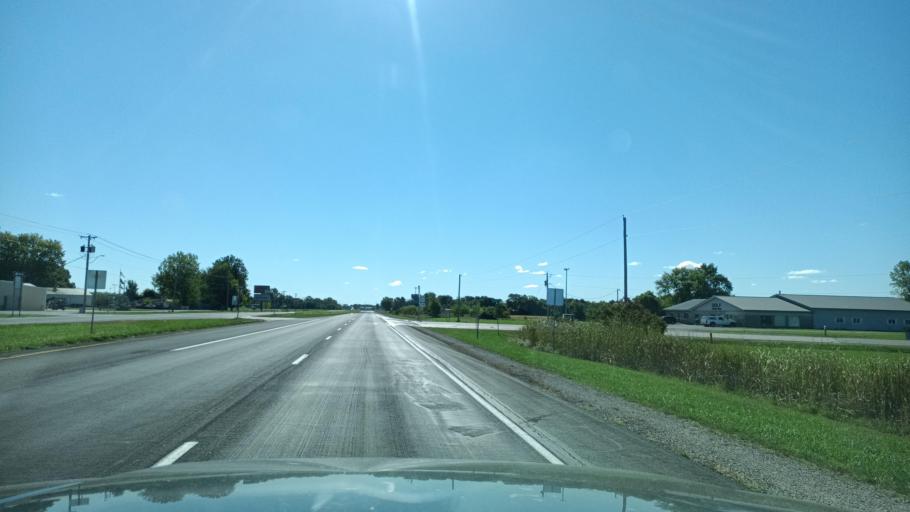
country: US
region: Iowa
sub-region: Lee County
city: Keokuk
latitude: 40.4447
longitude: -91.4393
